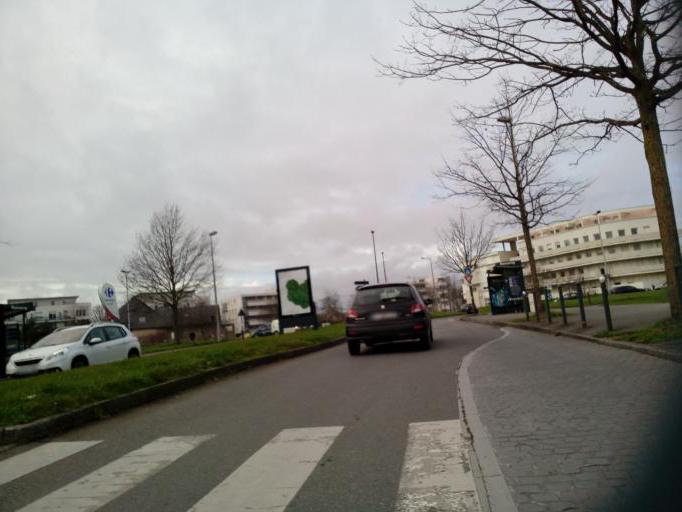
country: FR
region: Brittany
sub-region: Departement d'Ille-et-Vilaine
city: Chantepie
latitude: 48.0927
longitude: -1.6390
